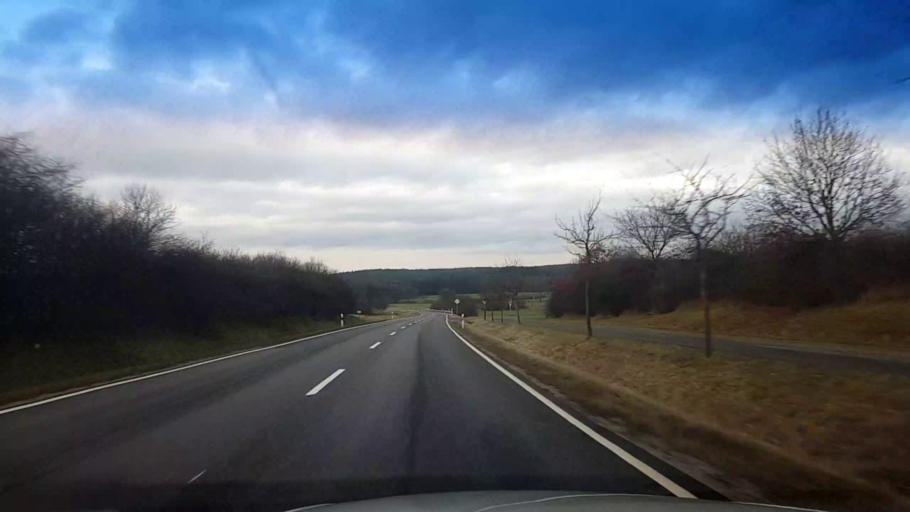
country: DE
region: Bavaria
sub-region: Upper Franconia
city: Litzendorf
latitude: 49.8829
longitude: 10.9963
